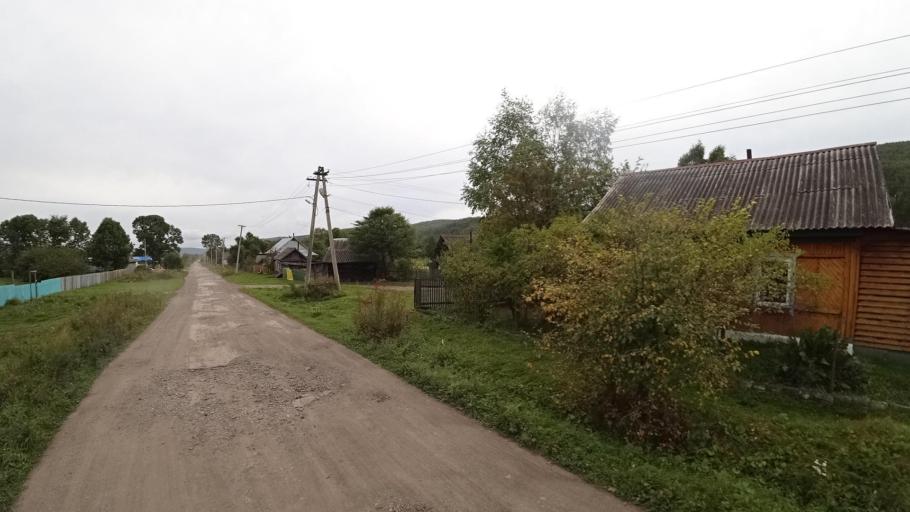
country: RU
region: Jewish Autonomous Oblast
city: Khingansk
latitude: 49.0395
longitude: 131.0497
